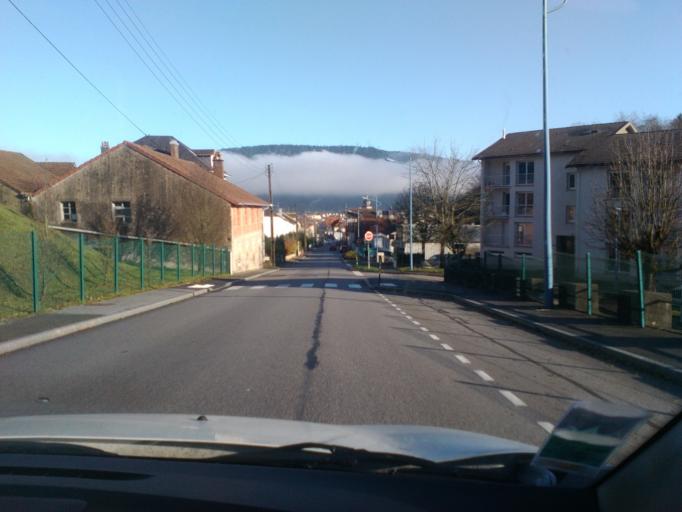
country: FR
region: Lorraine
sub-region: Departement des Vosges
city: Remiremont
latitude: 48.0102
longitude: 6.5829
